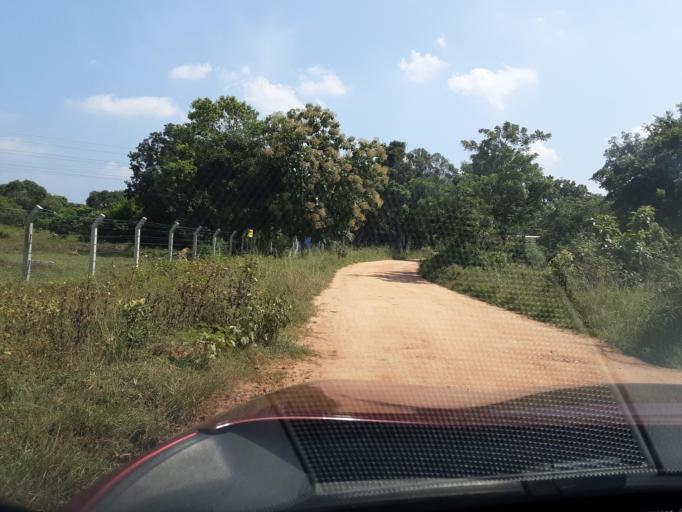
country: LK
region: Central
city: Sigiriya
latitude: 8.0055
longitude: 80.7459
